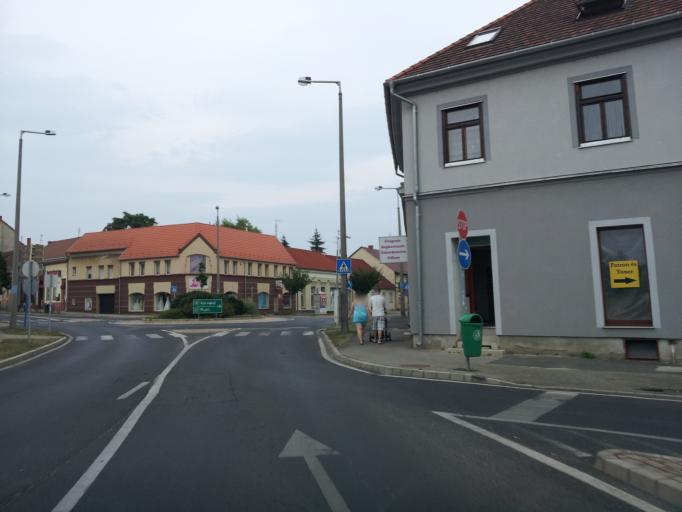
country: HU
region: Vas
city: Szombathely
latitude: 47.2281
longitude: 16.6191
